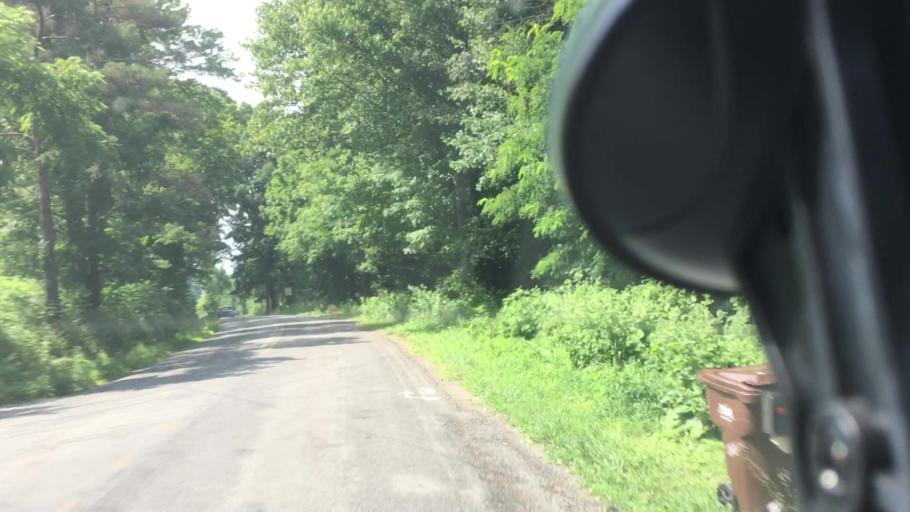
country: US
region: Pennsylvania
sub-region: Mercer County
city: Reynolds Heights
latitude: 41.3019
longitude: -80.3660
